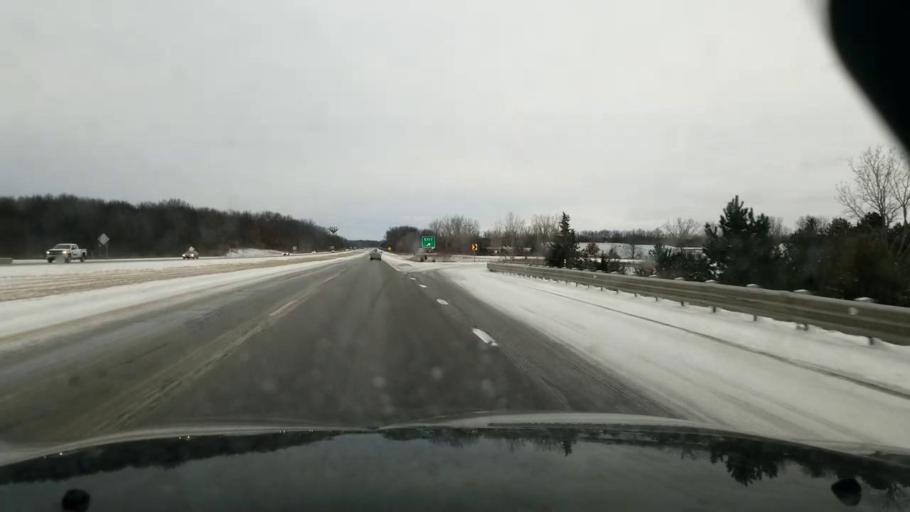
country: US
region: Michigan
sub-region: Jackson County
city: Jackson
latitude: 42.2540
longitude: -84.4764
